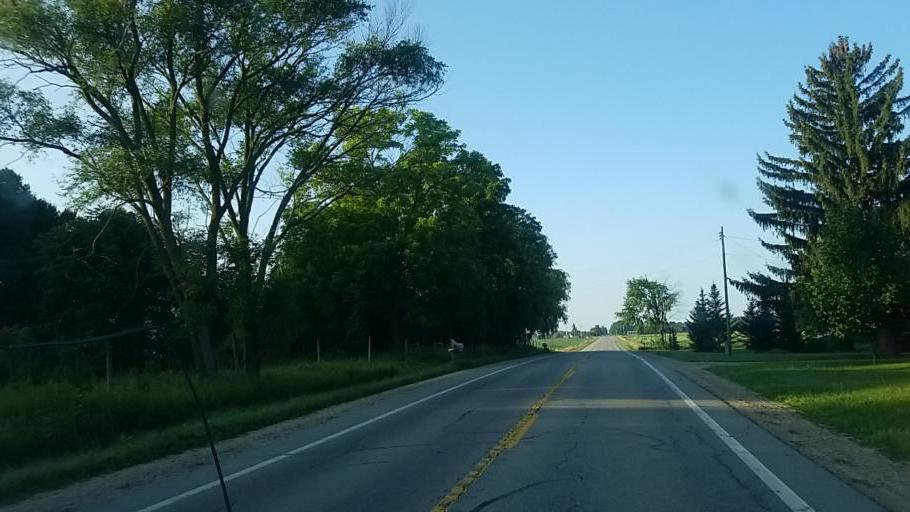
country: US
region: Michigan
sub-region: Montcalm County
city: Lakeview
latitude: 43.4184
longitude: -85.2633
